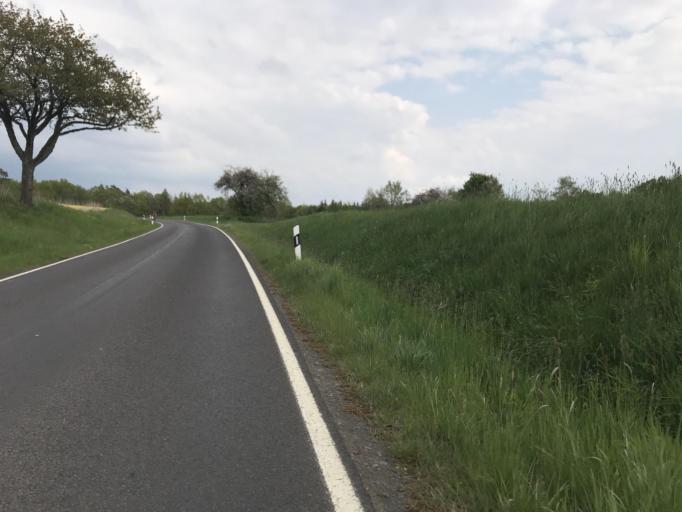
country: DE
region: Hesse
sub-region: Regierungsbezirk Giessen
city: Laubach
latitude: 50.5271
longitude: 8.9996
